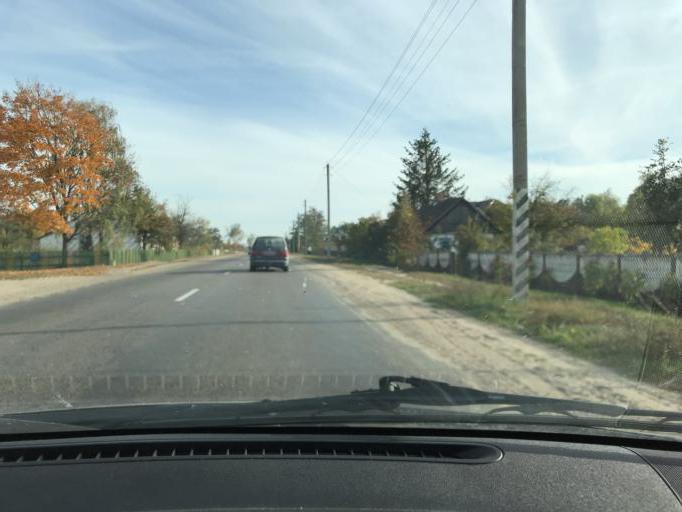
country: BY
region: Brest
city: Asnyezhytsy
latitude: 52.2253
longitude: 26.0259
